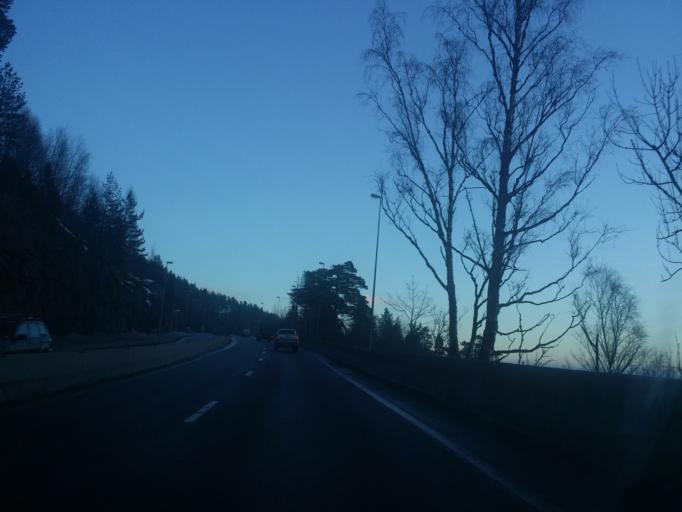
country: NO
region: Buskerud
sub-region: Hole
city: Vik
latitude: 59.9844
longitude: 10.3076
